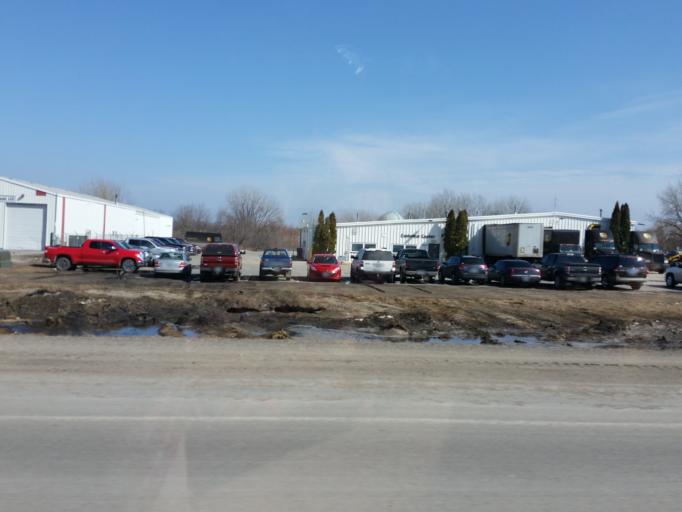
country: US
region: North Dakota
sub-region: Grand Forks County
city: Grand Forks
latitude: 47.9509
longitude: -97.0687
